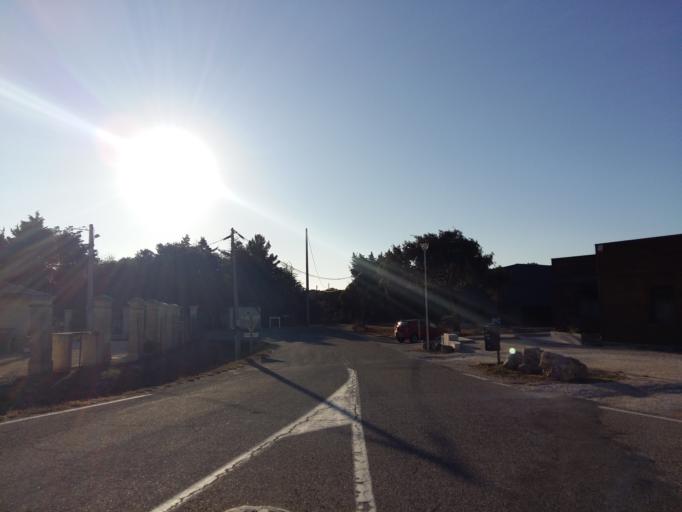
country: FR
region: Rhone-Alpes
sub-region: Departement de la Drome
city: Grignan
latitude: 44.4214
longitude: 4.8909
